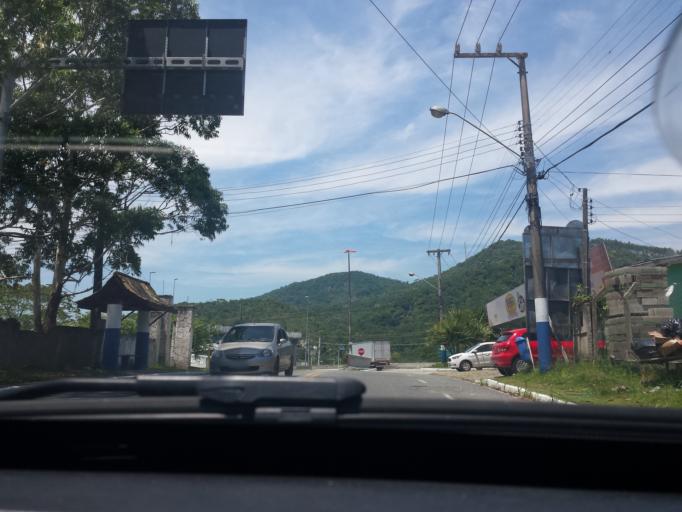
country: BR
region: Santa Catarina
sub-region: Itapema
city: Itapema
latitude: -27.0574
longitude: -48.5969
